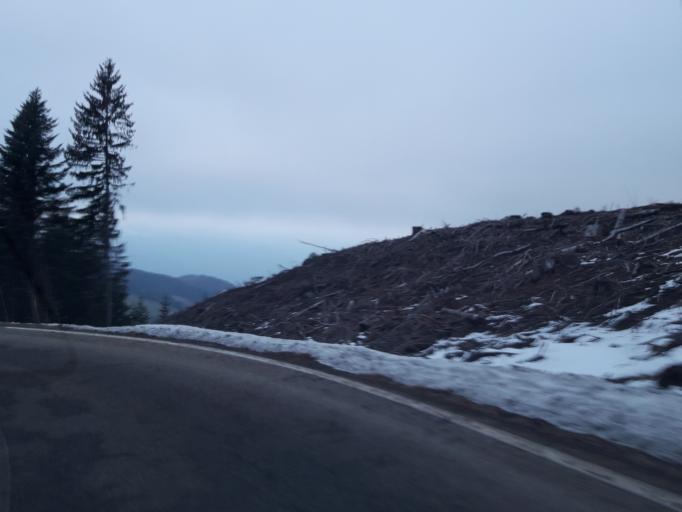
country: FR
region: Rhone-Alpes
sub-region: Departement de l'Isere
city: Theys
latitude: 45.2684
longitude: 5.9990
